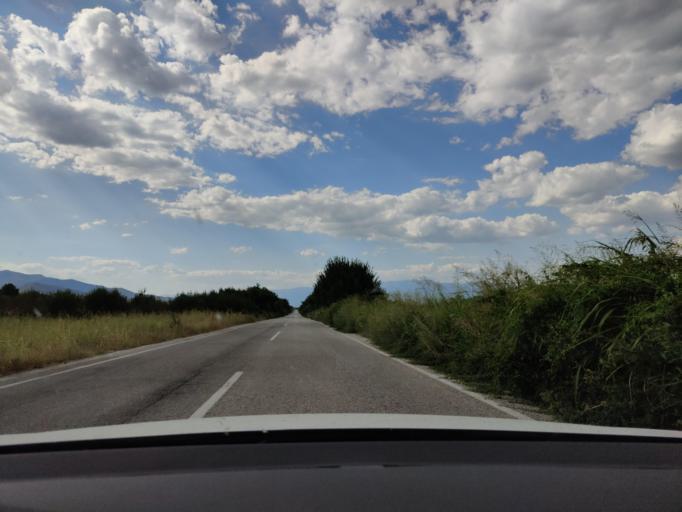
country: GR
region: Central Macedonia
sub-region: Nomos Serron
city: Strymoniko
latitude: 41.0671
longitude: 23.3047
